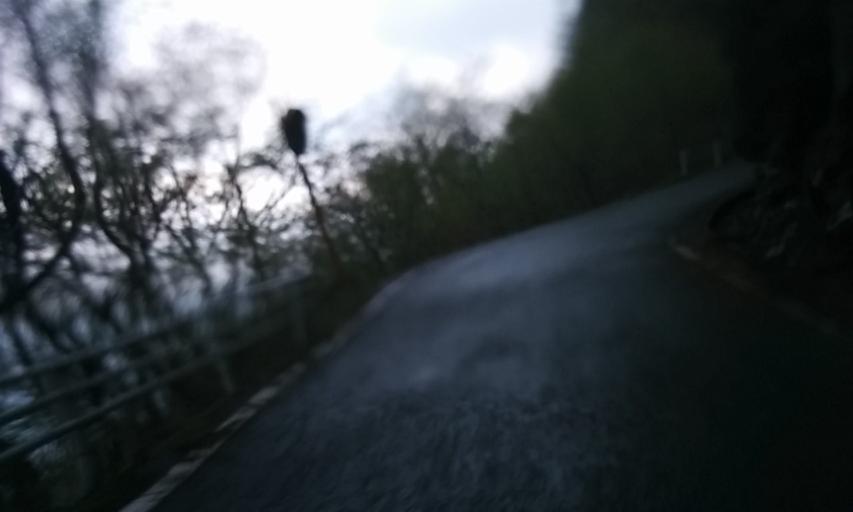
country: JP
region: Ehime
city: Saijo
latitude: 33.7848
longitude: 133.2791
